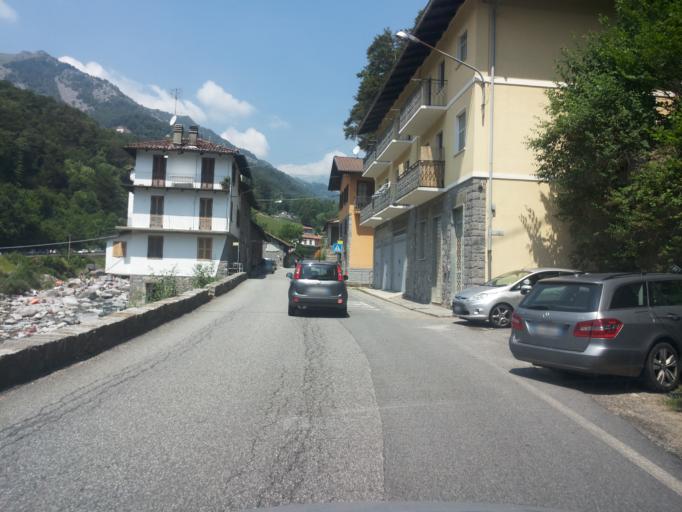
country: IT
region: Piedmont
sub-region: Provincia di Biella
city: San Paolo Cervo
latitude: 45.6550
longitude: 8.0104
